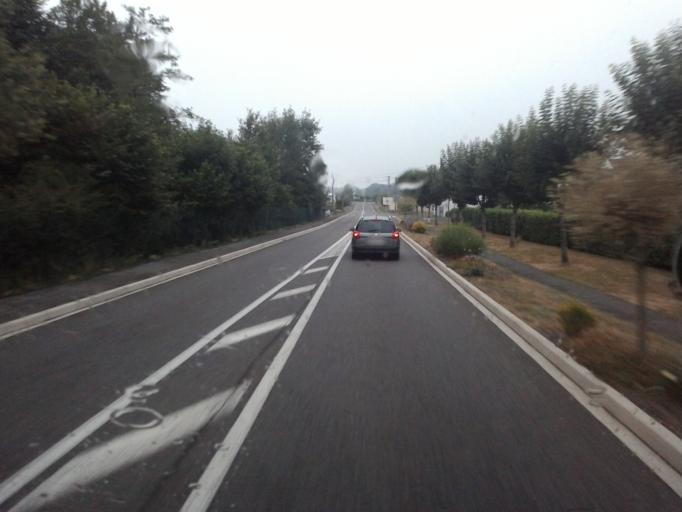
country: FR
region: Franche-Comte
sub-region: Departement de la Haute-Saone
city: Melisey
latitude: 47.7482
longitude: 6.5609
